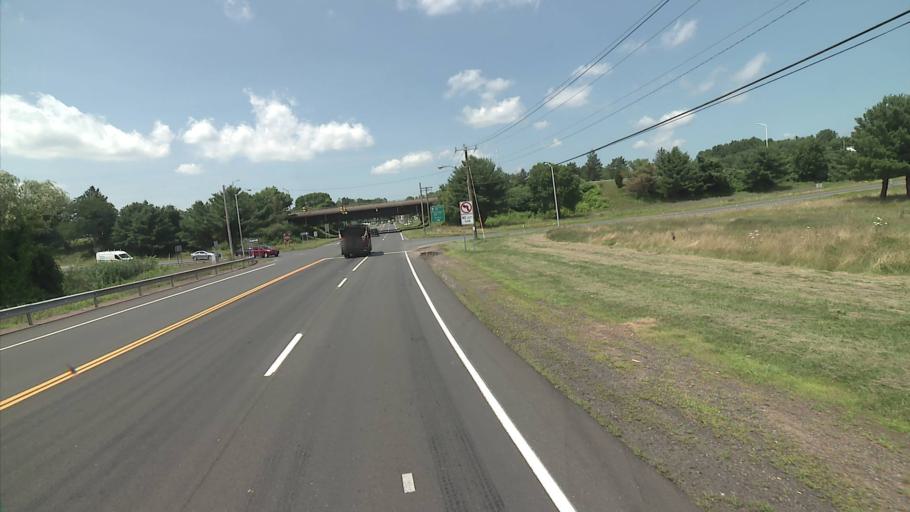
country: US
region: Connecticut
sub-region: Tolland County
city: Rockville
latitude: 41.8534
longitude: -72.4284
